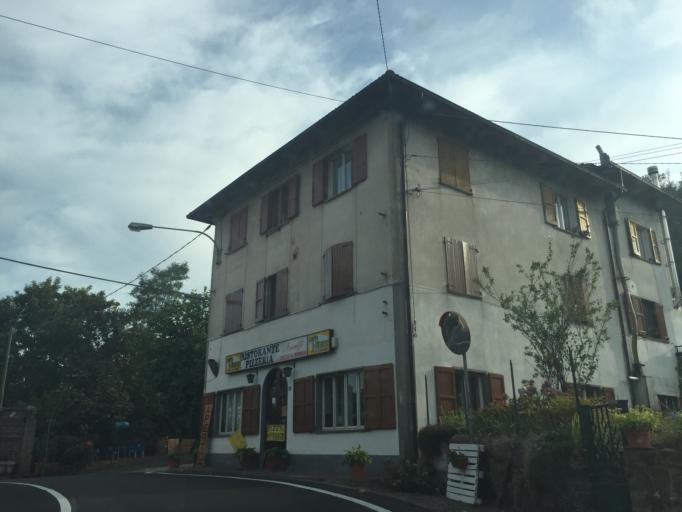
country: IT
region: Tuscany
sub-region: Provincia di Pistoia
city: Campo Tizzoro
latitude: 44.0028
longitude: 10.8343
